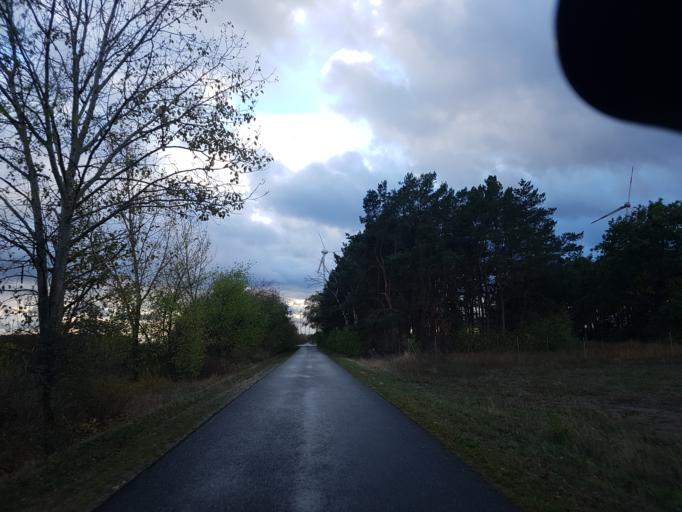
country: DE
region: Saxony-Anhalt
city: Seyda
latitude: 51.8431
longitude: 12.8905
